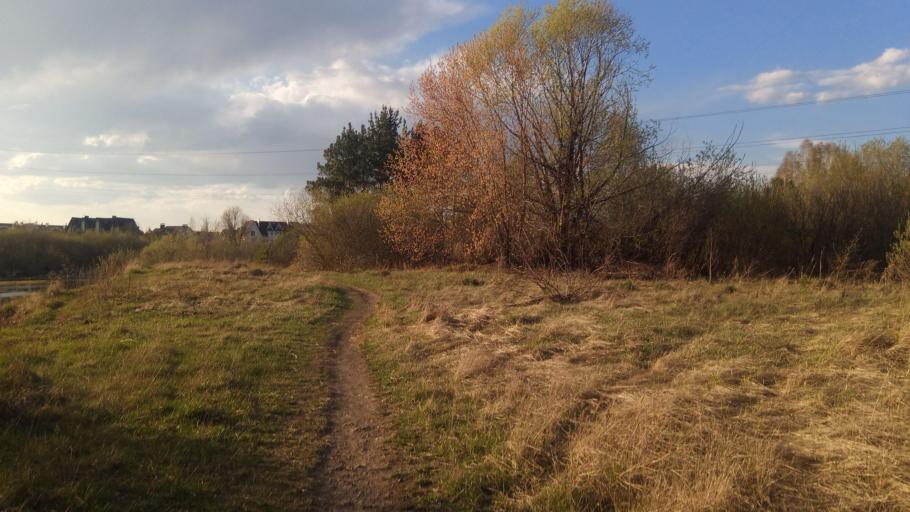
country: RU
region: Chelyabinsk
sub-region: Gorod Chelyabinsk
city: Chelyabinsk
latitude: 55.1530
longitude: 61.3222
